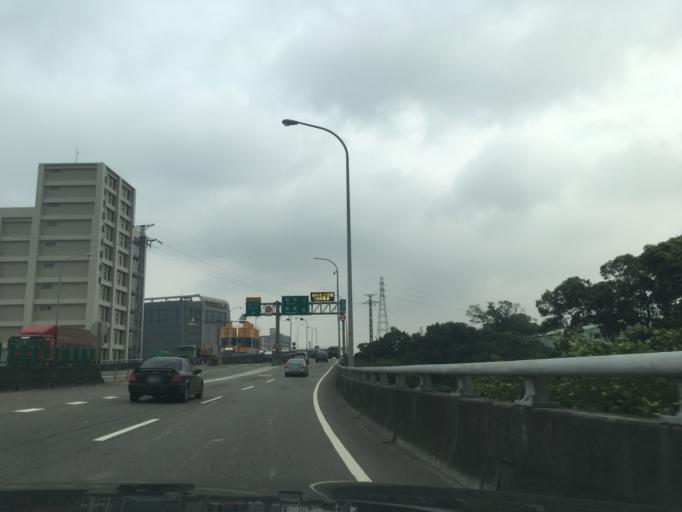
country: TW
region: Taipei
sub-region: Taipei
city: Banqiao
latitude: 24.9670
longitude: 121.4328
